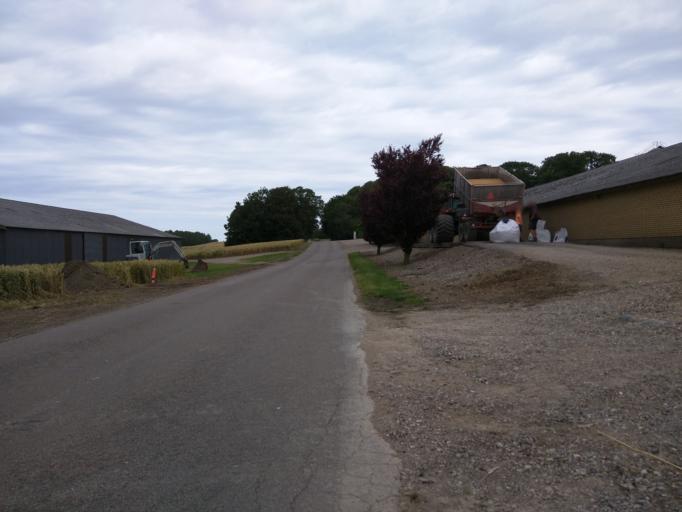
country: DK
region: Zealand
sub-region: Kalundborg Kommune
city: Svebolle
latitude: 55.6965
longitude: 11.3065
